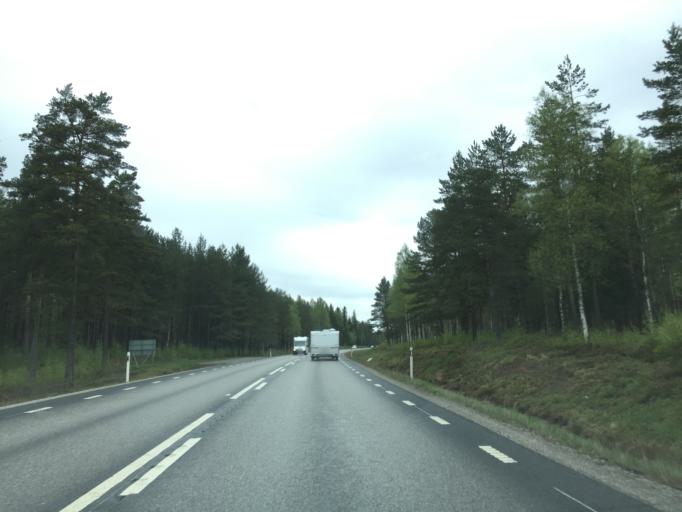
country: SE
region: OErebro
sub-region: Lindesbergs Kommun
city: Lindesberg
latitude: 59.6113
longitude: 15.1845
